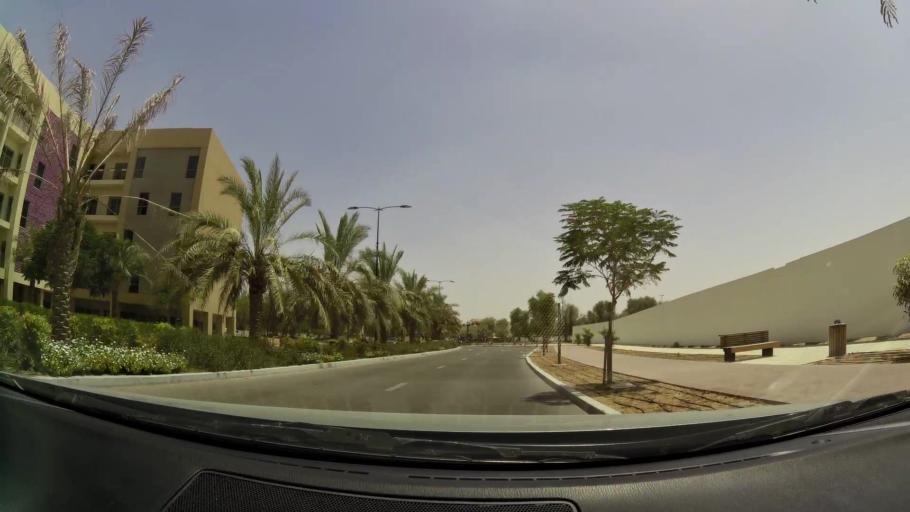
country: AE
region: Abu Dhabi
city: Al Ain
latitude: 24.2438
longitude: 55.7142
